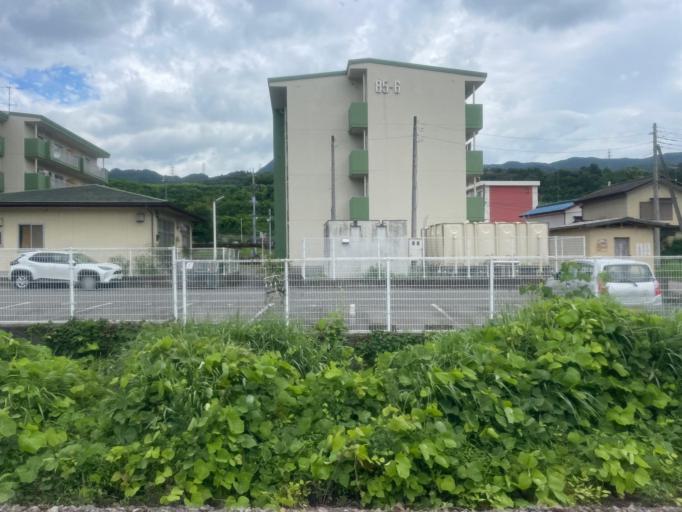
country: JP
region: Gunma
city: Numata
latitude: 36.7037
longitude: 138.9810
